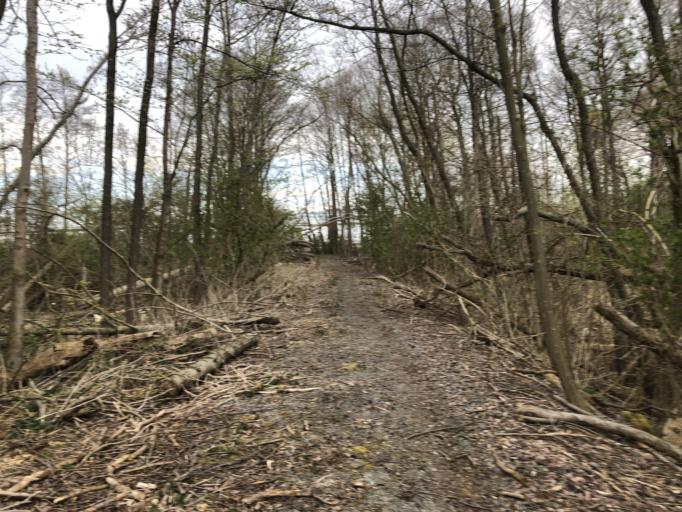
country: SE
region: Skane
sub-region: Malmo
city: Oxie
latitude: 55.5544
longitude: 13.0545
